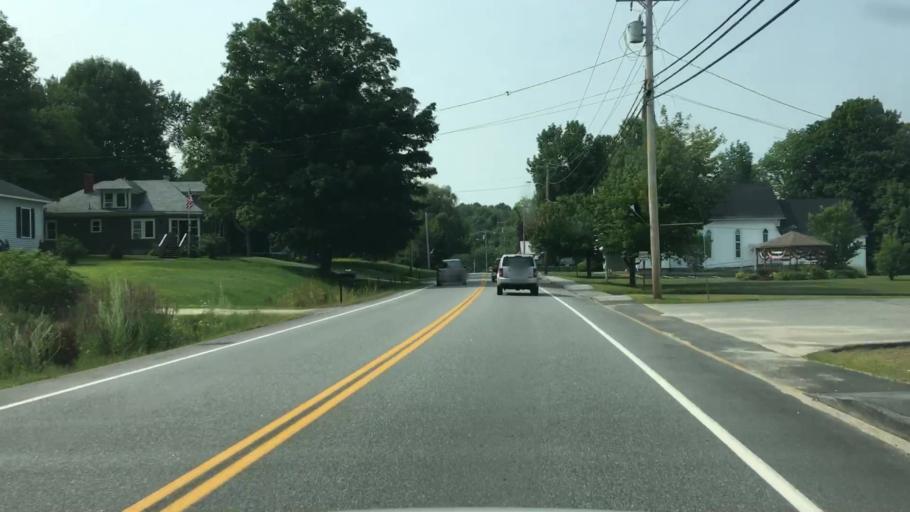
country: US
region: Maine
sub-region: Oxford County
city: Buckfield
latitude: 44.2882
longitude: -70.3621
